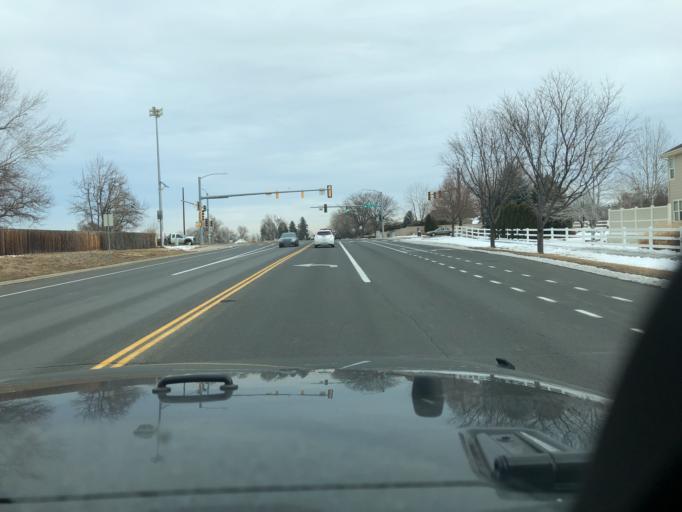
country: US
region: Colorado
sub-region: Boulder County
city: Longmont
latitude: 40.1740
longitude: -105.0754
